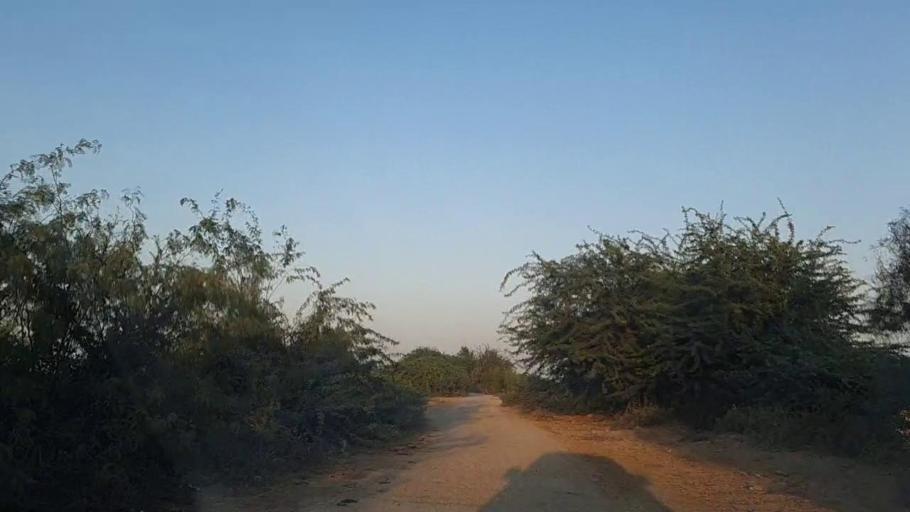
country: PK
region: Sindh
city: Chuhar Jamali
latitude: 24.4499
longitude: 68.1175
